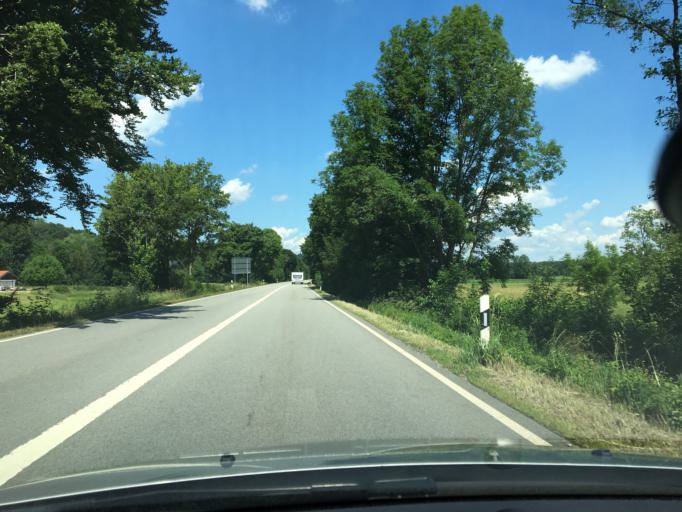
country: DE
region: Bavaria
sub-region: Upper Bavaria
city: Laufen
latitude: 47.9042
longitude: 12.9456
